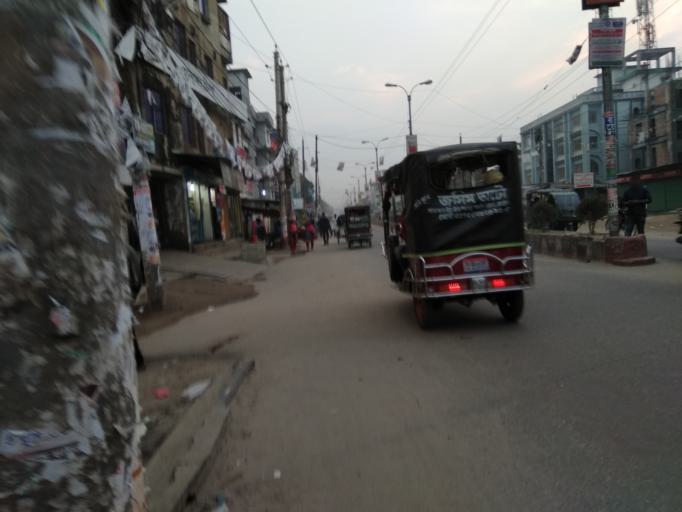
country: BD
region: Rangpur Division
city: Rangpur
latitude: 25.7327
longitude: 89.2548
